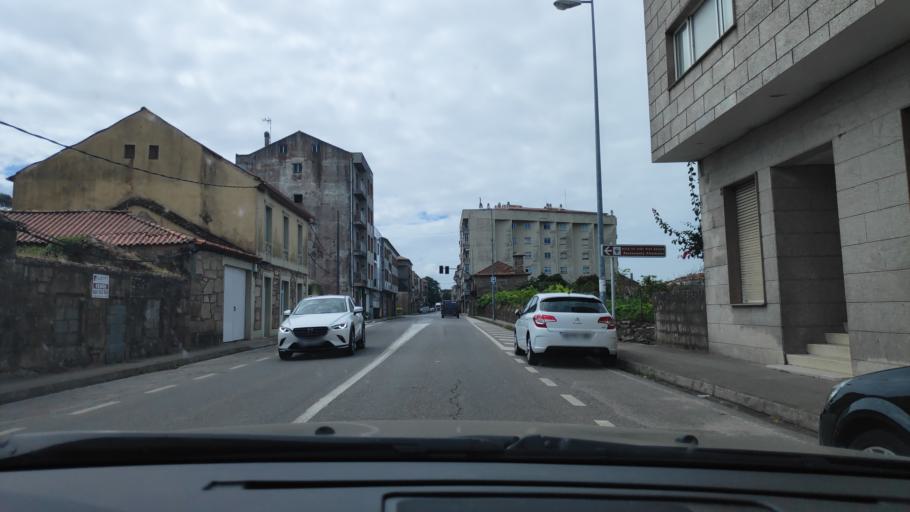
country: ES
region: Galicia
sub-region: Provincia de Pontevedra
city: Cambados
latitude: 42.5235
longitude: -8.8124
